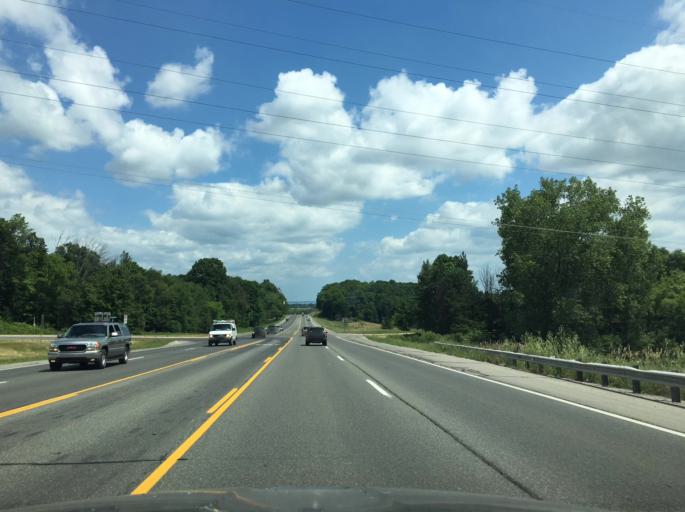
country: US
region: Michigan
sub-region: Grand Traverse County
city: Traverse City
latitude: 44.7073
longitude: -85.6523
